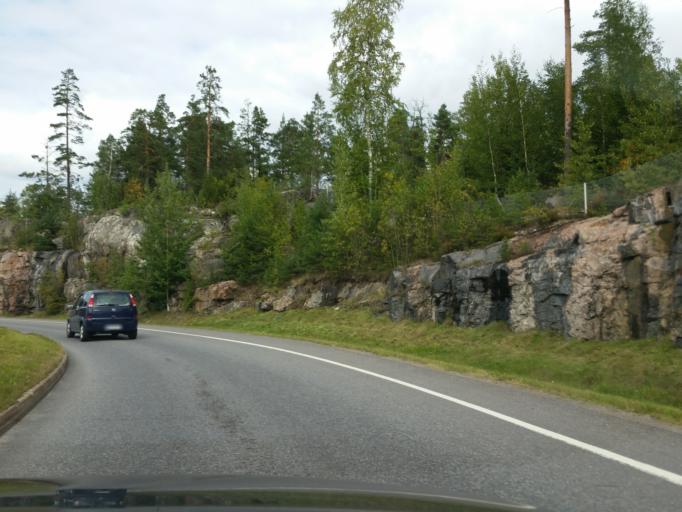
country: FI
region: Uusimaa
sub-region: Helsinki
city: Vantaa
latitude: 60.3070
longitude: 24.9684
